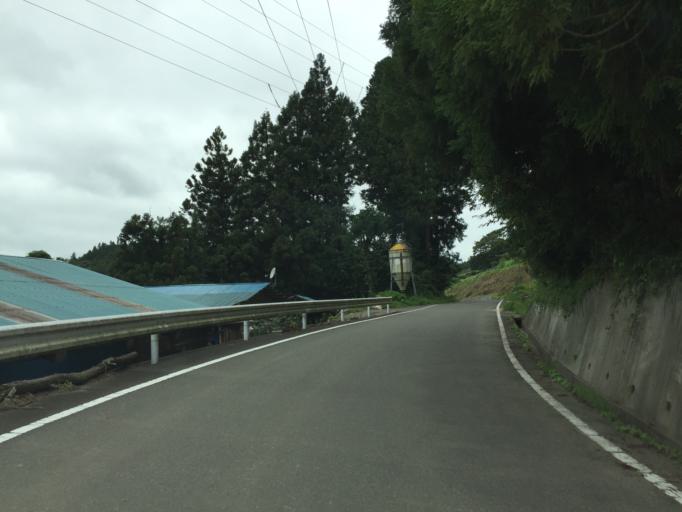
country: JP
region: Fukushima
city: Ishikawa
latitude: 37.2062
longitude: 140.5994
